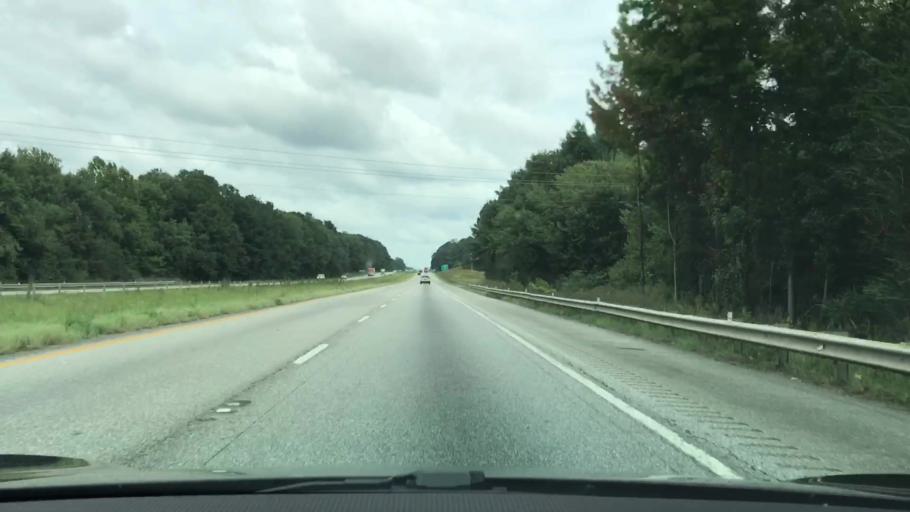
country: US
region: Alabama
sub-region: Chambers County
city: Huguley
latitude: 32.8026
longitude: -85.2300
